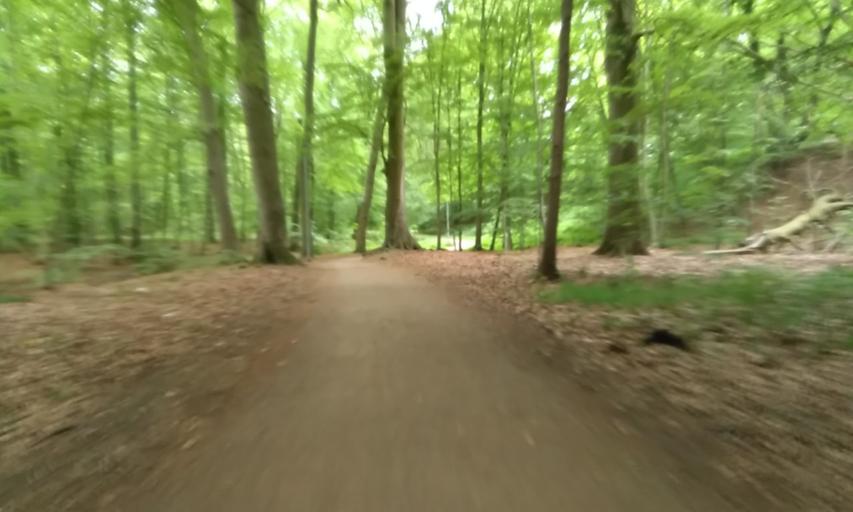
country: DE
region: Lower Saxony
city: Harsefeld
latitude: 53.4510
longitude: 9.4916
